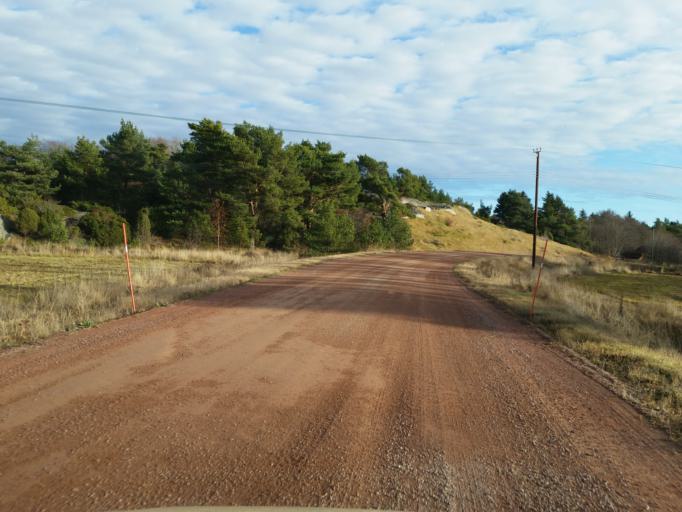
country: AX
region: Alands skaergard
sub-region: Kumlinge
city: Kumlinge
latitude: 60.2572
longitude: 20.7862
